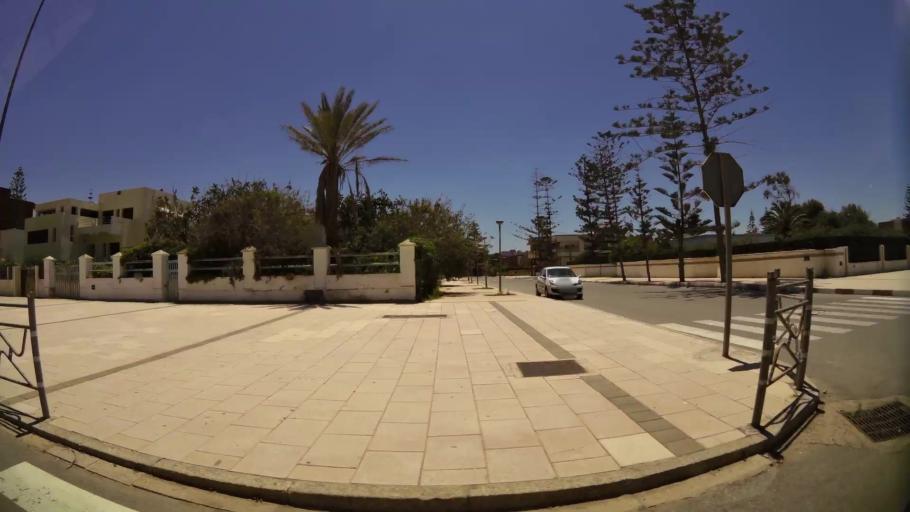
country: MA
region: Oriental
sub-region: Berkane-Taourirt
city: Madagh
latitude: 35.0875
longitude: -2.2295
